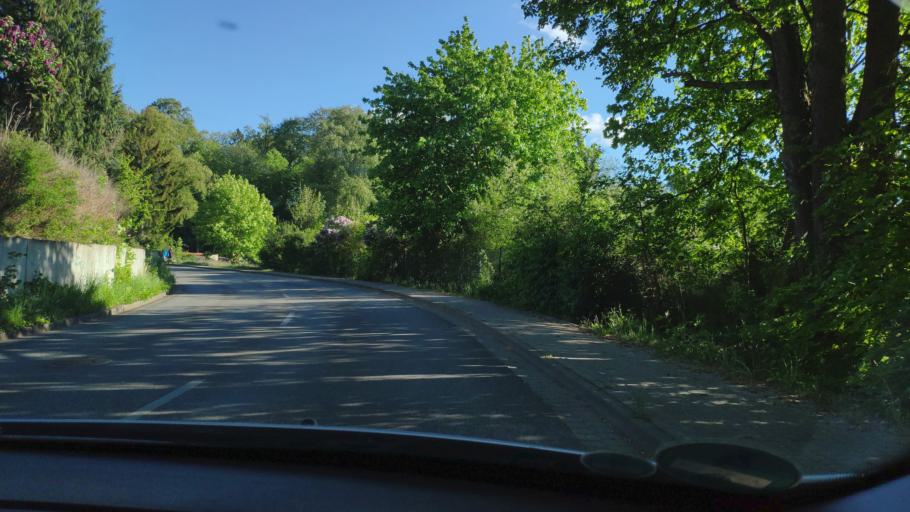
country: DE
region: Mecklenburg-Vorpommern
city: Neustrelitz
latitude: 53.3553
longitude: 13.0512
